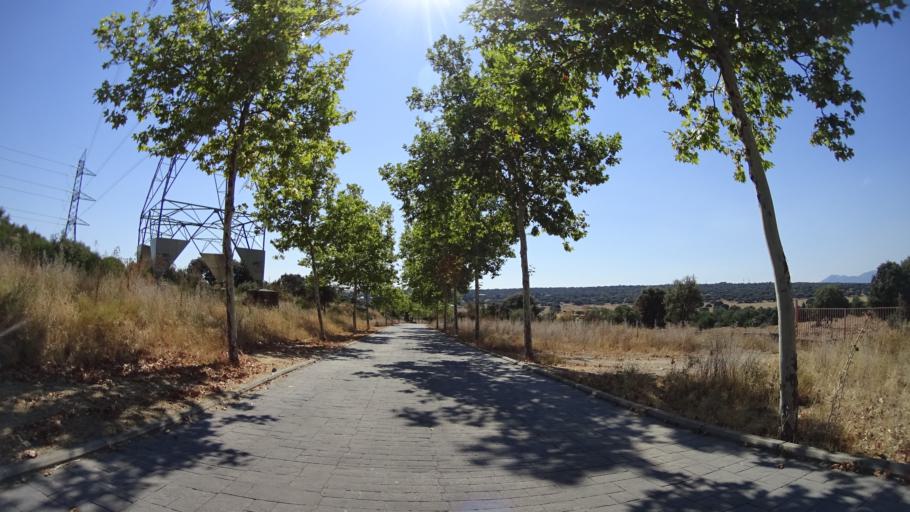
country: ES
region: Madrid
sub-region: Provincia de Madrid
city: Galapagar
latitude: 40.5946
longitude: -4.0105
